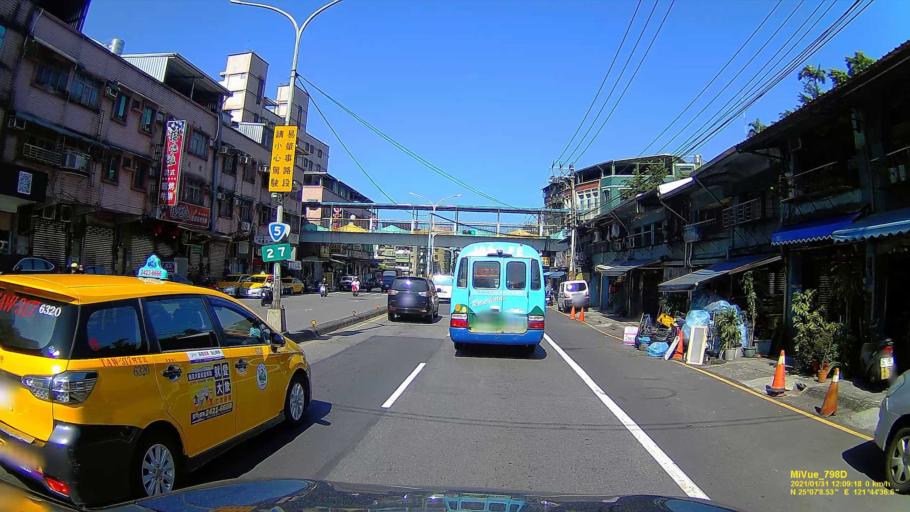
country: TW
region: Taiwan
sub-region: Keelung
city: Keelung
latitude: 25.1191
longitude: 121.7435
